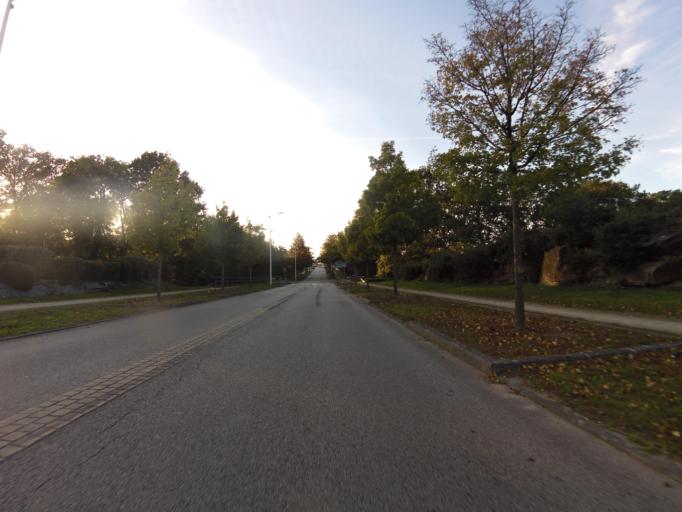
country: FR
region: Brittany
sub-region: Departement du Morbihan
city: Theix
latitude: 47.6287
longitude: -2.6457
